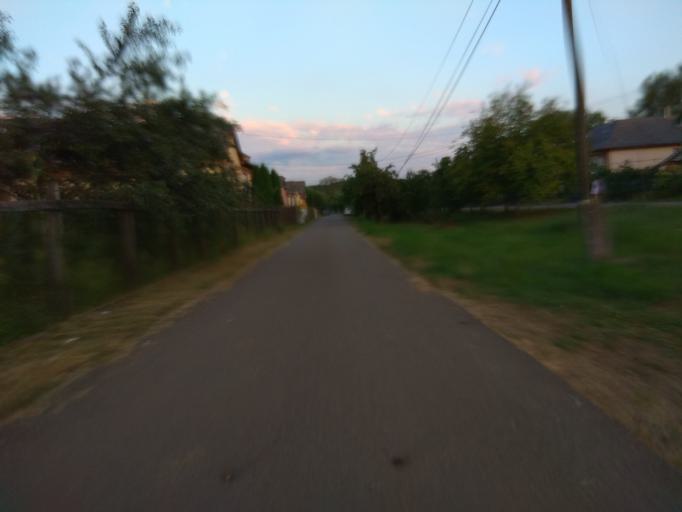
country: HU
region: Heves
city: Tarnalelesz
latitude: 48.0512
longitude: 20.1562
